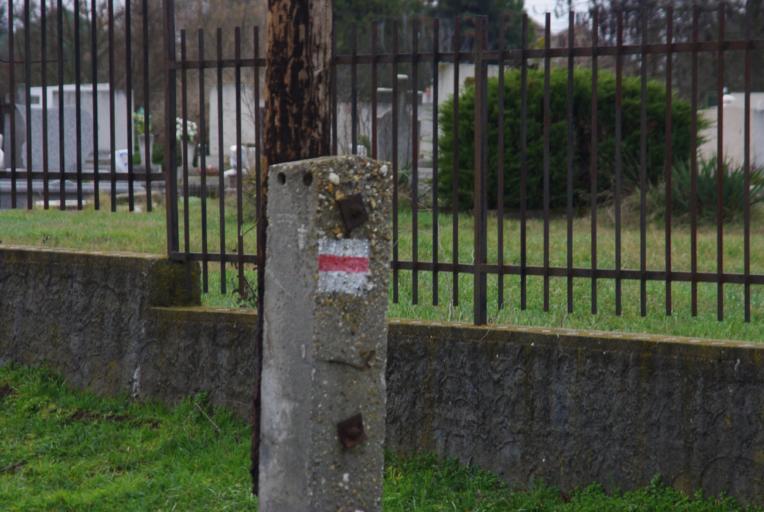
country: HU
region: Pest
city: Szod
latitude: 47.7176
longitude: 19.1921
